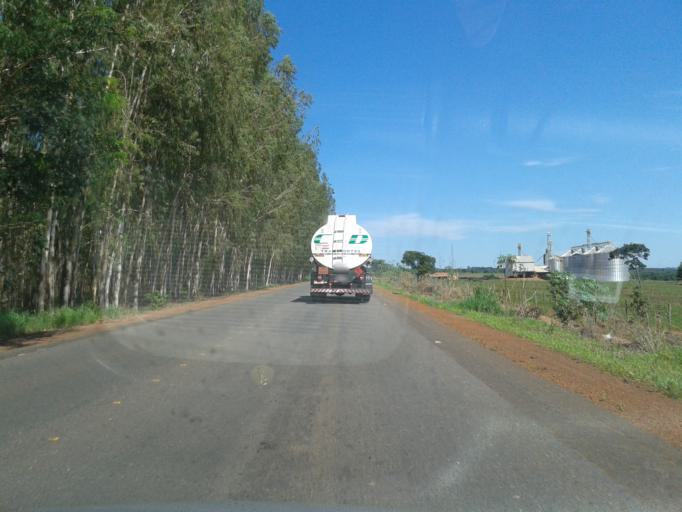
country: BR
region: Goias
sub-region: Bela Vista De Goias
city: Bela Vista de Goias
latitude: -17.0433
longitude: -48.9423
